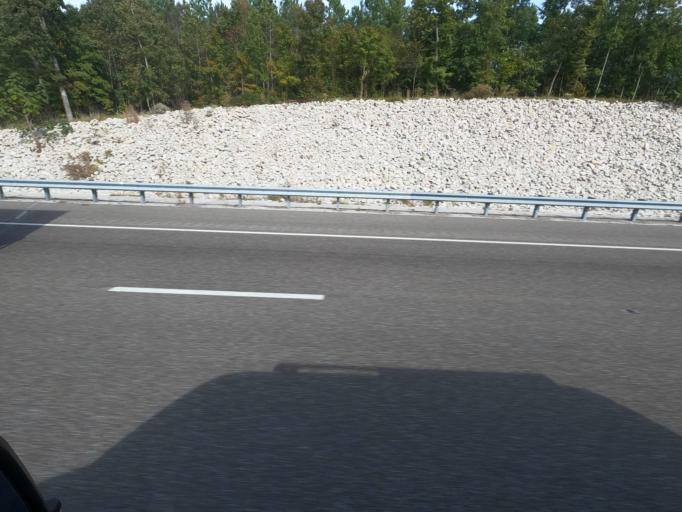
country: US
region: Tennessee
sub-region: Humphreys County
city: New Johnsonville
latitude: 35.8687
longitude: -87.9830
